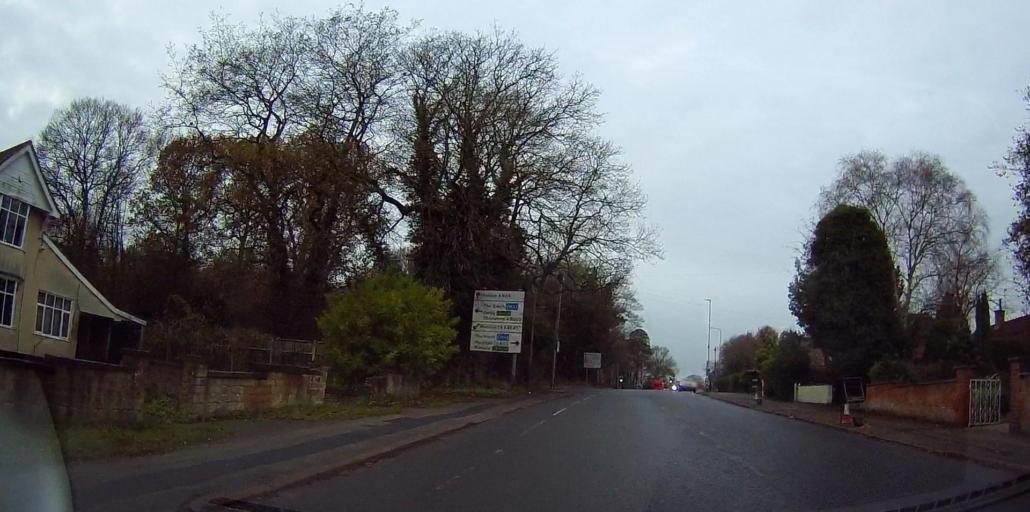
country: GB
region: England
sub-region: Nottinghamshire
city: Kimberley
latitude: 52.9552
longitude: -1.2441
